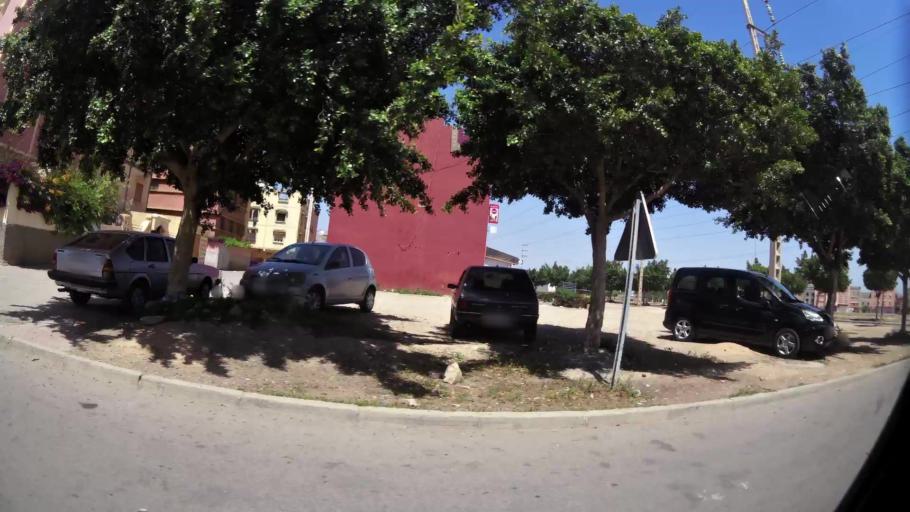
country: MA
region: Souss-Massa-Draa
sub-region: Inezgane-Ait Mellou
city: Inezgane
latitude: 30.3462
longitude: -9.4890
